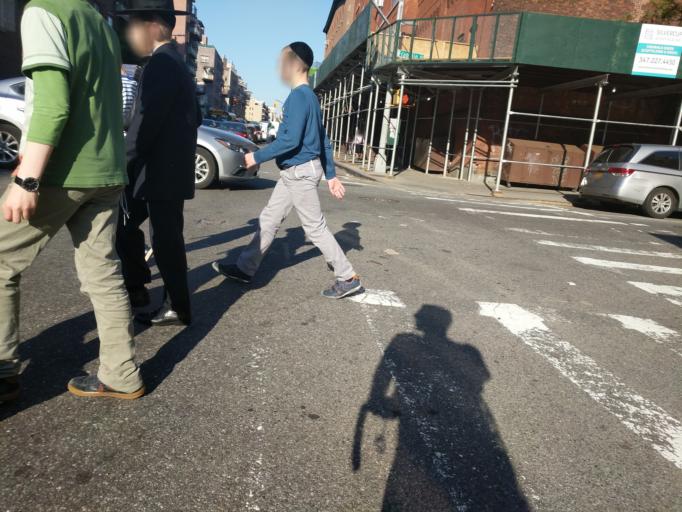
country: US
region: New York
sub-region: Queens County
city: Long Island City
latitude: 40.6986
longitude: -73.9590
